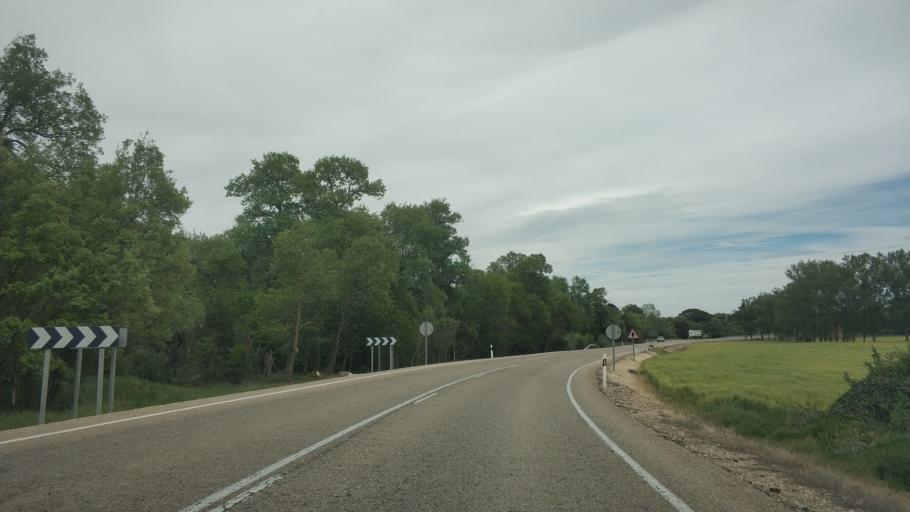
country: ES
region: Castille and Leon
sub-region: Provincia de Soria
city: Bayubas de Abajo
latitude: 41.5047
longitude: -2.8940
